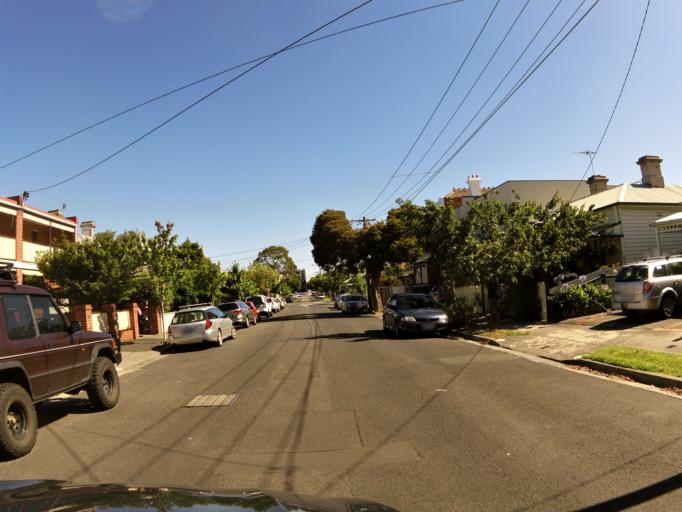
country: AU
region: Victoria
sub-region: Yarra
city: Richmond
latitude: -37.8239
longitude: 145.0059
